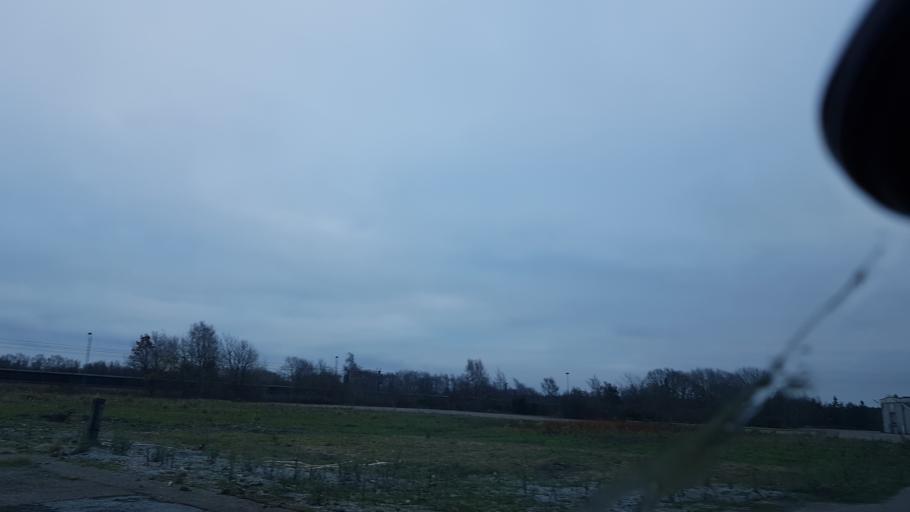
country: DK
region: South Denmark
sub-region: Haderslev Kommune
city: Vojens
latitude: 55.2428
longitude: 9.3027
